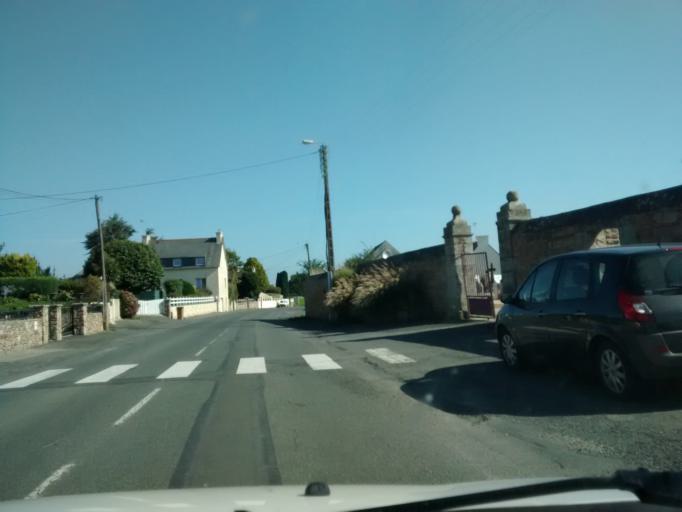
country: FR
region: Brittany
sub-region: Departement des Cotes-d'Armor
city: Pleubian
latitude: 48.8453
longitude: -3.1361
